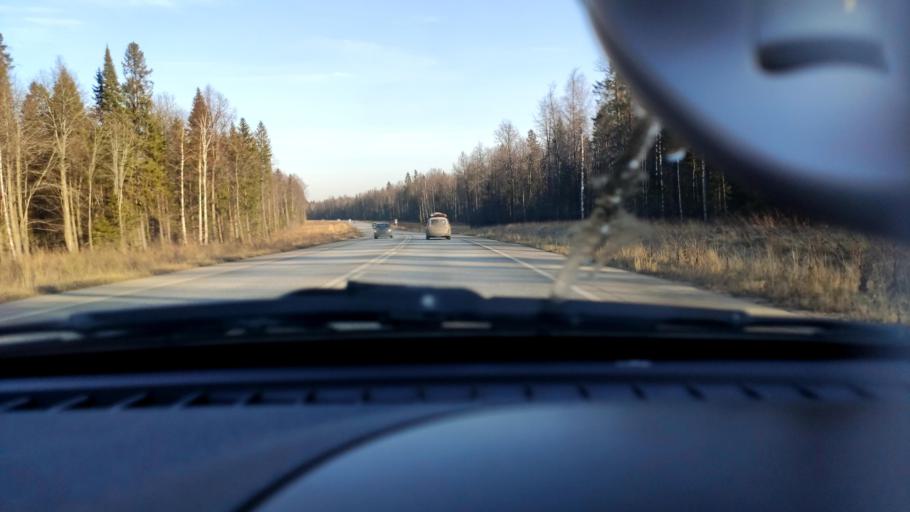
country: RU
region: Perm
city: Novyye Lyady
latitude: 58.0324
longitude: 56.5285
